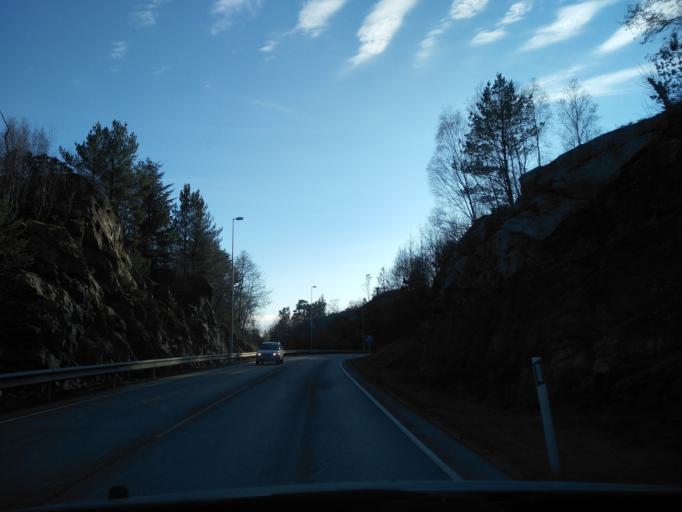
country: NO
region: Rogaland
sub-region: Tysvaer
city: Aksdal
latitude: 59.5035
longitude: 5.5864
